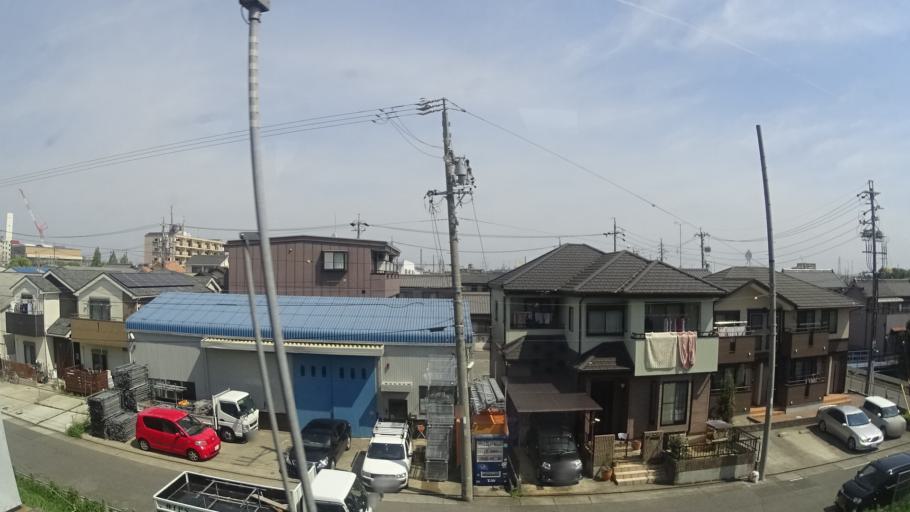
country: JP
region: Aichi
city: Kanie
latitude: 35.1441
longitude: 136.8213
